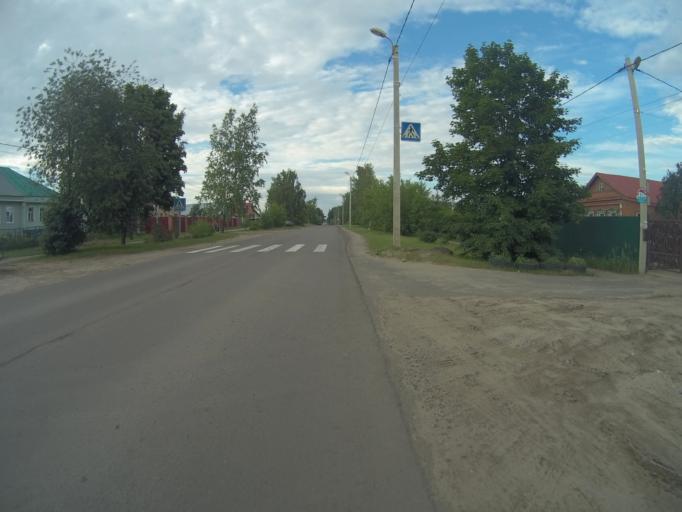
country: RU
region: Vladimir
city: Kommunar
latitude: 56.1096
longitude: 40.4459
